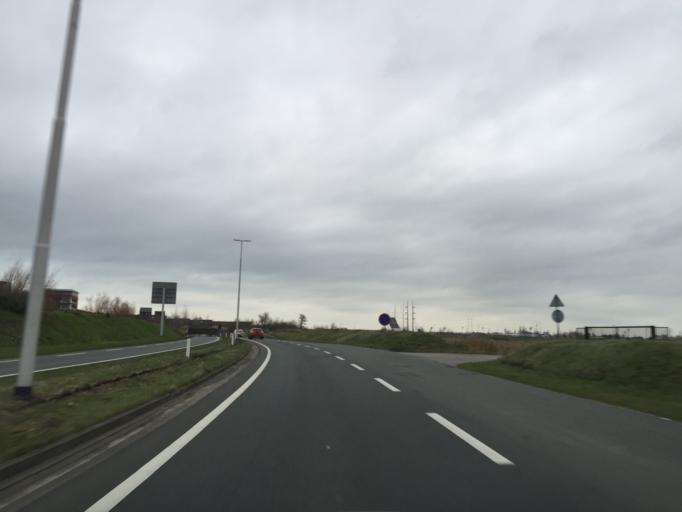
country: NL
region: South Holland
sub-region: Gemeente Lansingerland
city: Berkel en Rodenrijs
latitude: 52.0038
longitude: 4.4561
